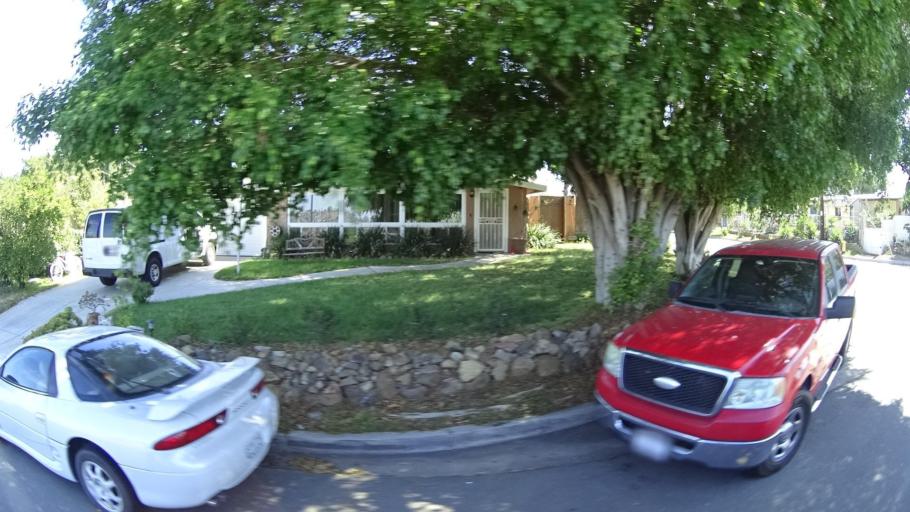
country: US
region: California
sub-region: San Diego County
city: La Presa
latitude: 32.7031
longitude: -117.0050
